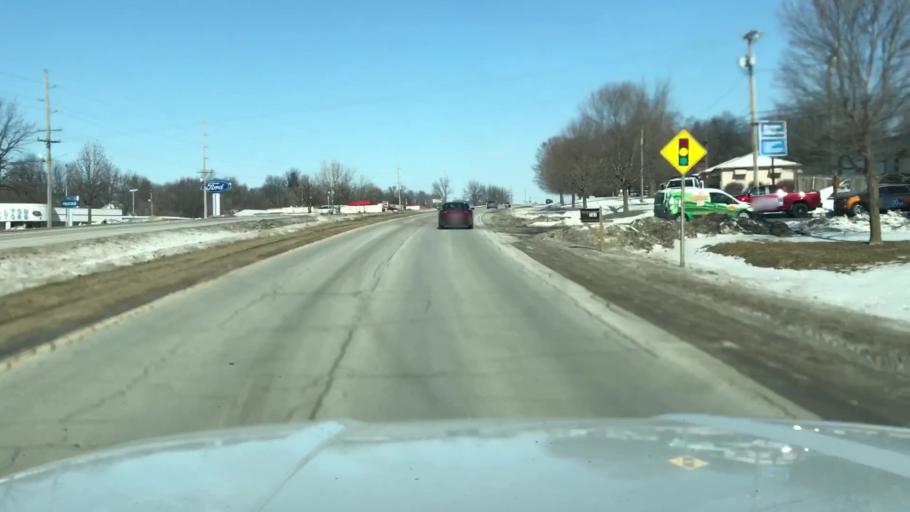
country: US
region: Missouri
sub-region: Andrew County
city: Savannah
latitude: 39.9346
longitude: -94.8214
